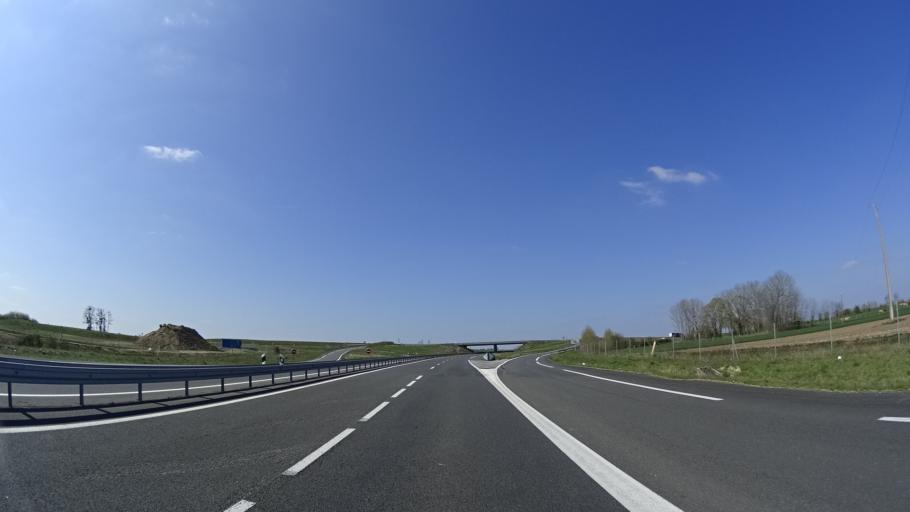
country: FR
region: Pays de la Loire
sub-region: Departement de Maine-et-Loire
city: Saint-Jean
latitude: 47.2860
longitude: -0.3689
